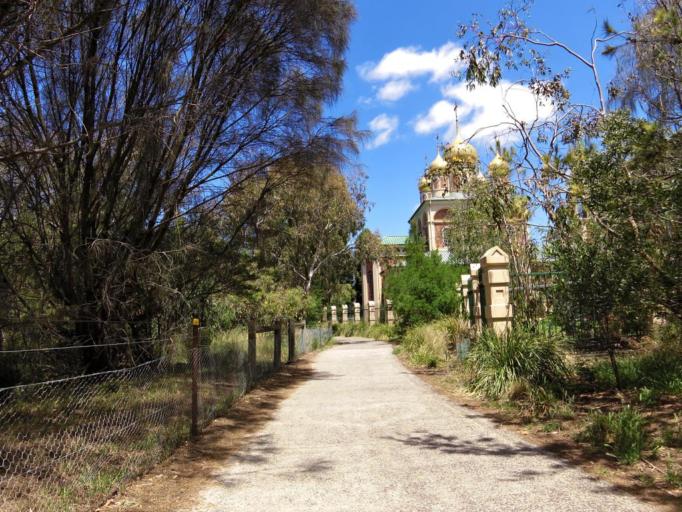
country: AU
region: Victoria
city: Brunswick East
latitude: -37.7622
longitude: 144.9812
